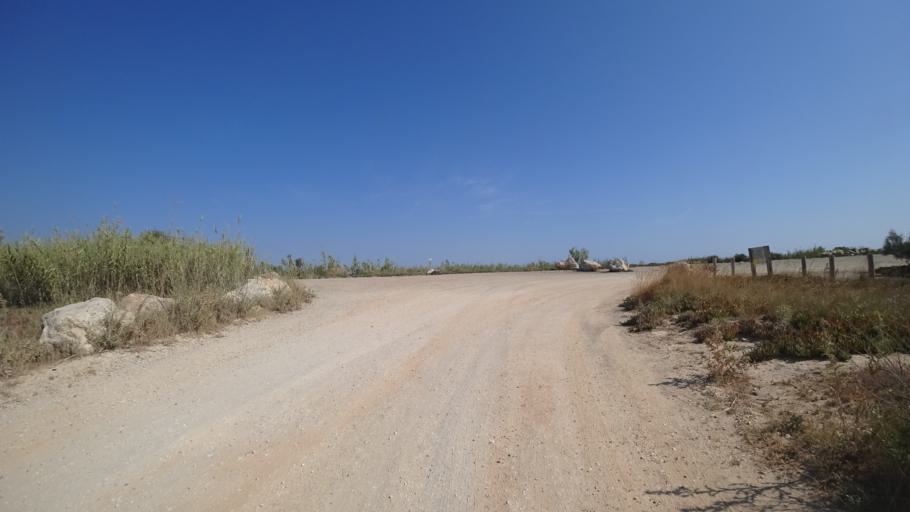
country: FR
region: Languedoc-Roussillon
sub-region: Departement des Pyrenees-Orientales
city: Le Barcares
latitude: 42.7779
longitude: 3.0371
